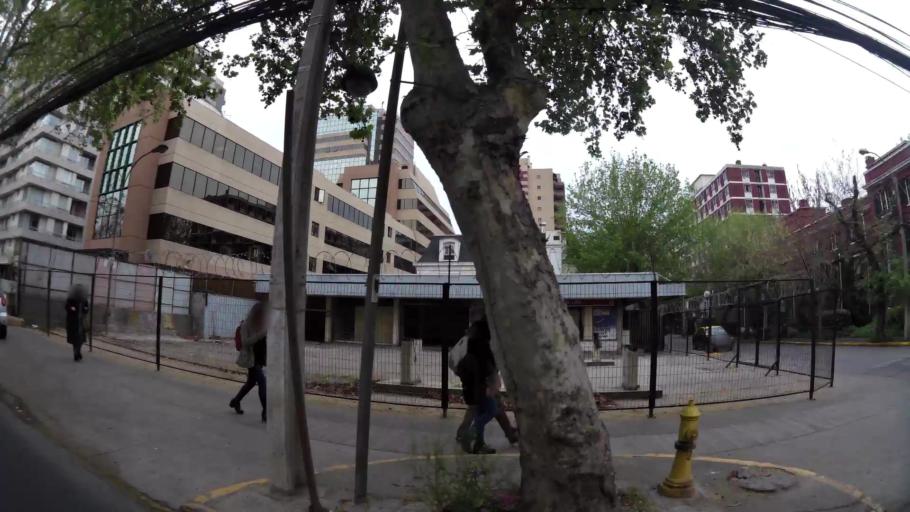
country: CL
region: Santiago Metropolitan
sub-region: Provincia de Santiago
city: Villa Presidente Frei, Nunoa, Santiago, Chile
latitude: -33.4207
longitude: -70.6118
